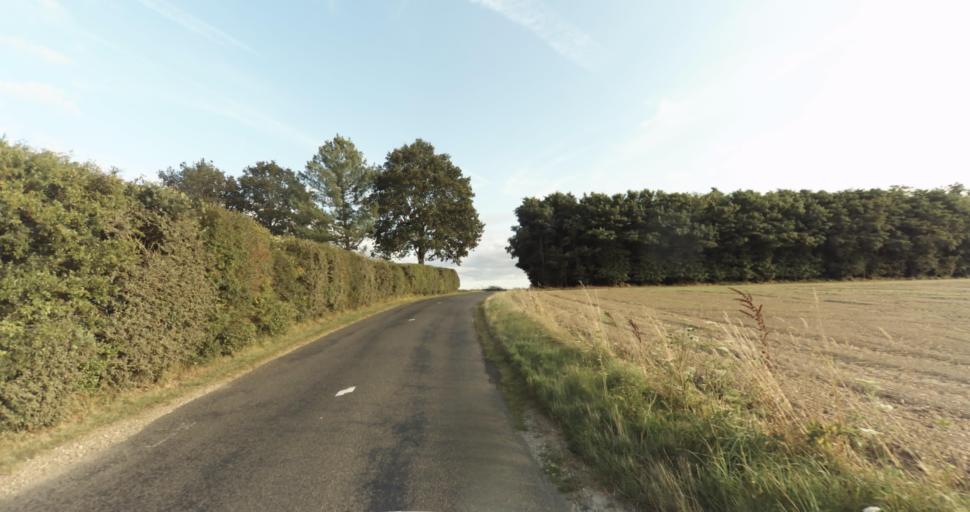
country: FR
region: Haute-Normandie
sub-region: Departement de l'Eure
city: Marcilly-sur-Eure
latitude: 48.8340
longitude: 1.2852
